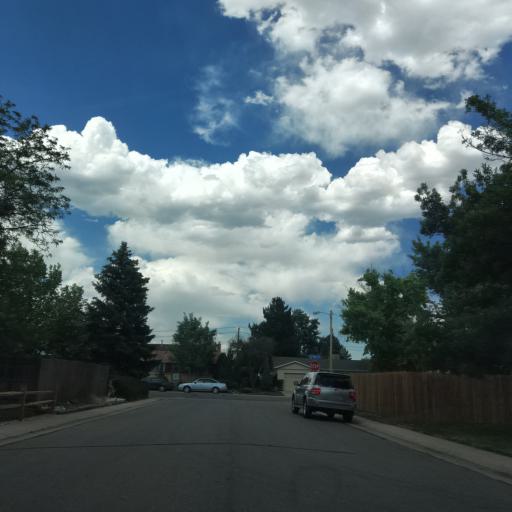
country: US
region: Colorado
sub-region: Jefferson County
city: Lakewood
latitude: 39.6871
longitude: -105.0993
